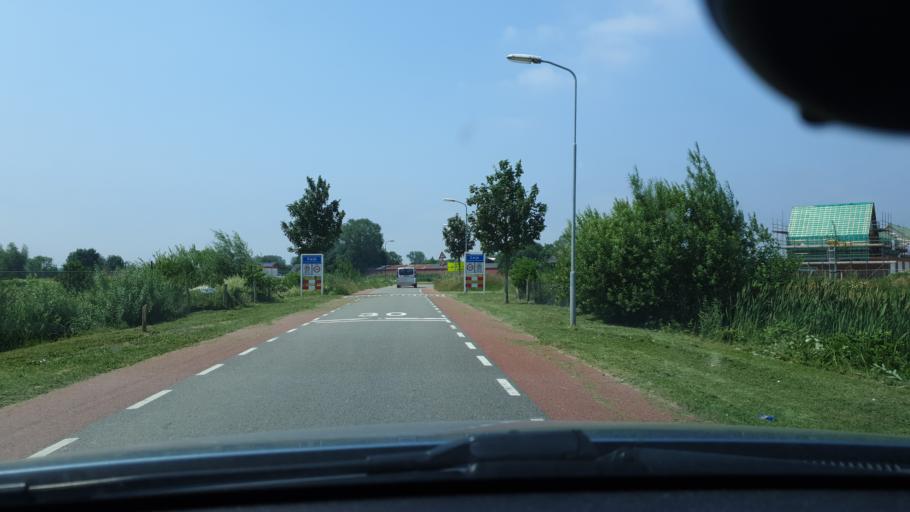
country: NL
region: Gelderland
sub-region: Gemeente Beuningen
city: Beuningen
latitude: 51.8632
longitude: 5.7479
